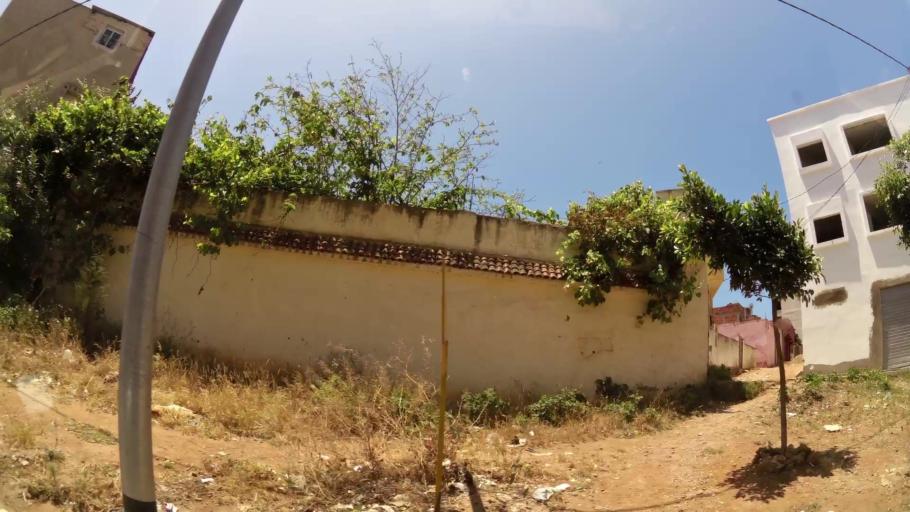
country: MA
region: Gharb-Chrarda-Beni Hssen
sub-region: Kenitra Province
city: Kenitra
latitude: 34.2652
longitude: -6.6437
